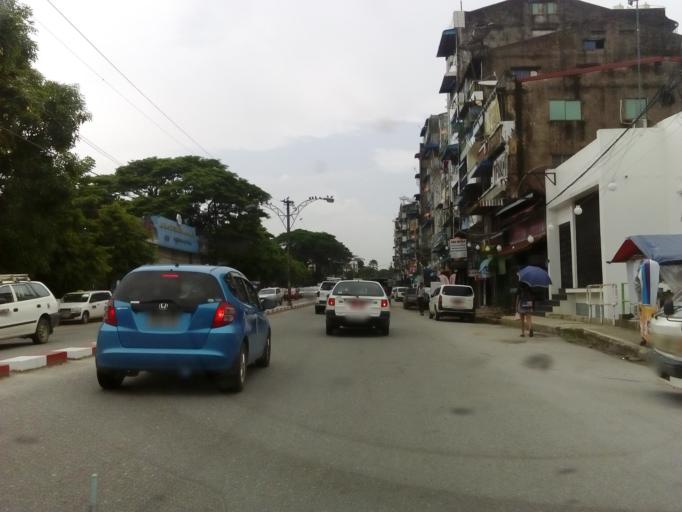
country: MM
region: Yangon
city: Yangon
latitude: 16.8049
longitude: 96.1734
